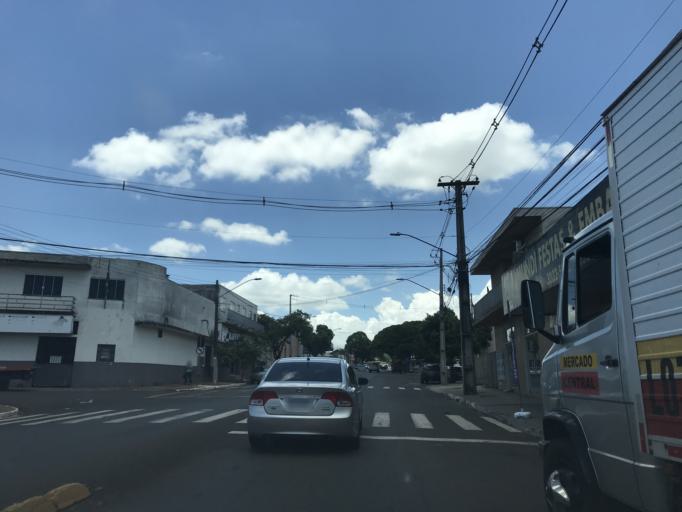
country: BR
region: Parana
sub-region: Marialva
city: Marialva
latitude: -23.4831
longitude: -51.8004
